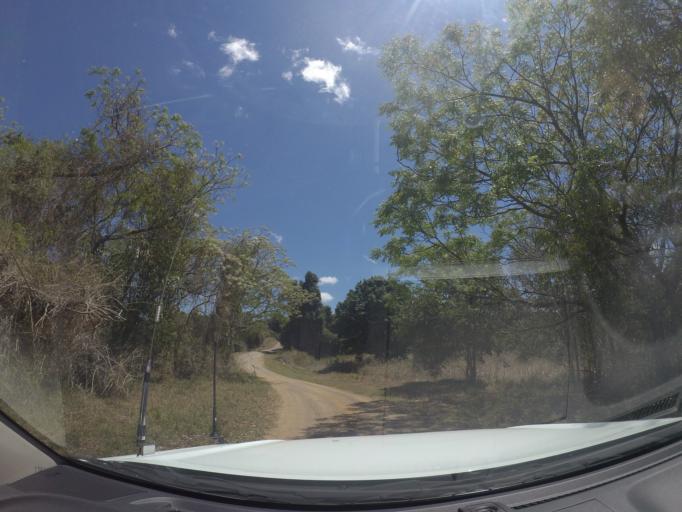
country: AU
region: Queensland
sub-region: Ipswich
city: Deebing Heights
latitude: -27.8296
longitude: 152.8185
